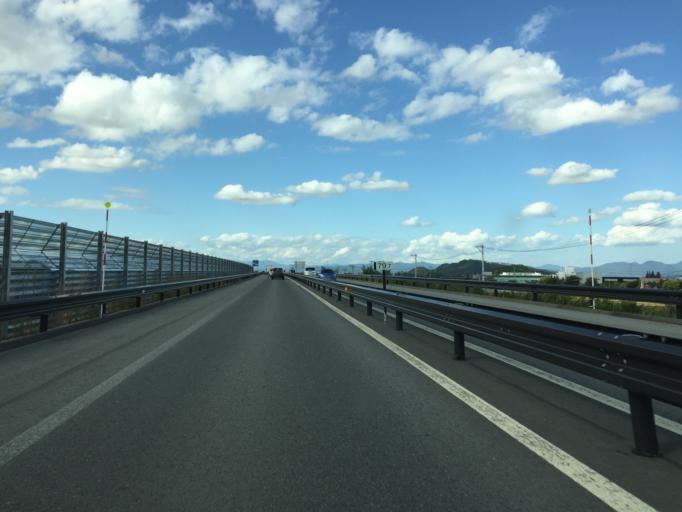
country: JP
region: Yamagata
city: Yonezawa
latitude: 37.9067
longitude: 140.1426
